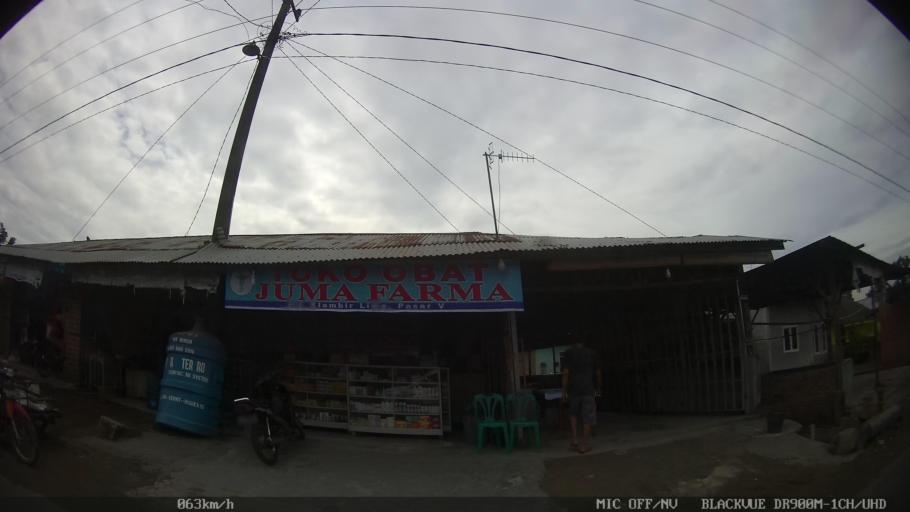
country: ID
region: North Sumatra
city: Sunggal
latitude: 3.6519
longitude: 98.5951
